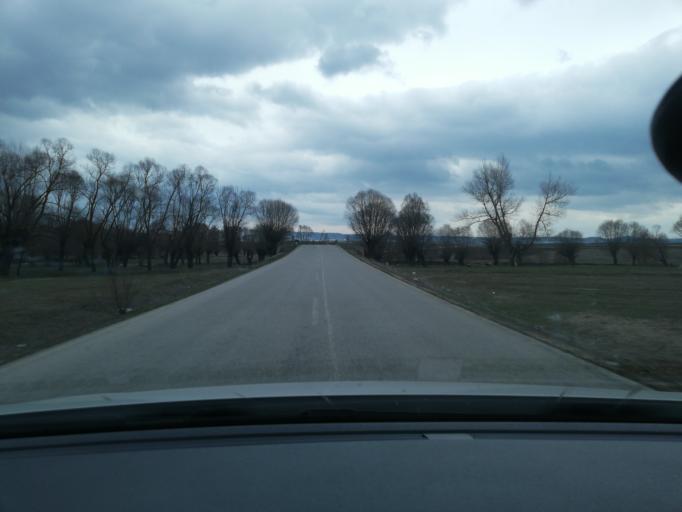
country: TR
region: Bolu
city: Gerede
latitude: 40.7284
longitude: 32.2201
